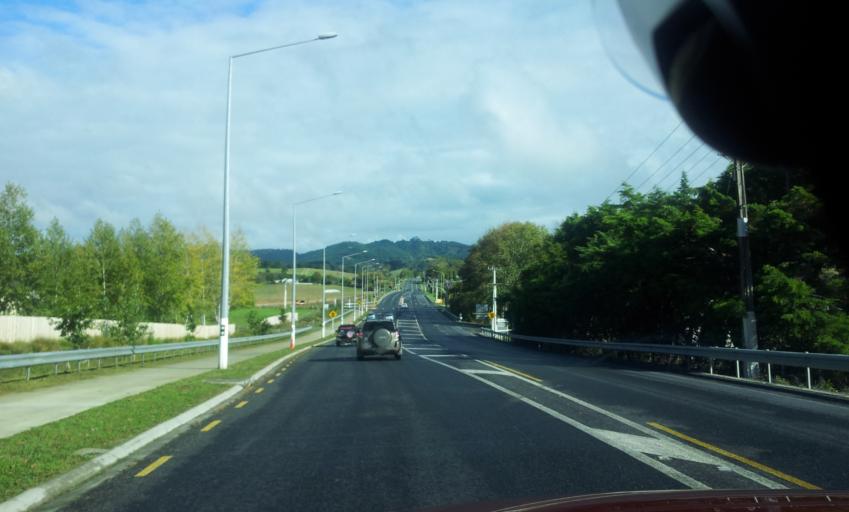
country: NZ
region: Auckland
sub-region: Auckland
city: Warkworth
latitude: -36.3929
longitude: 174.6538
